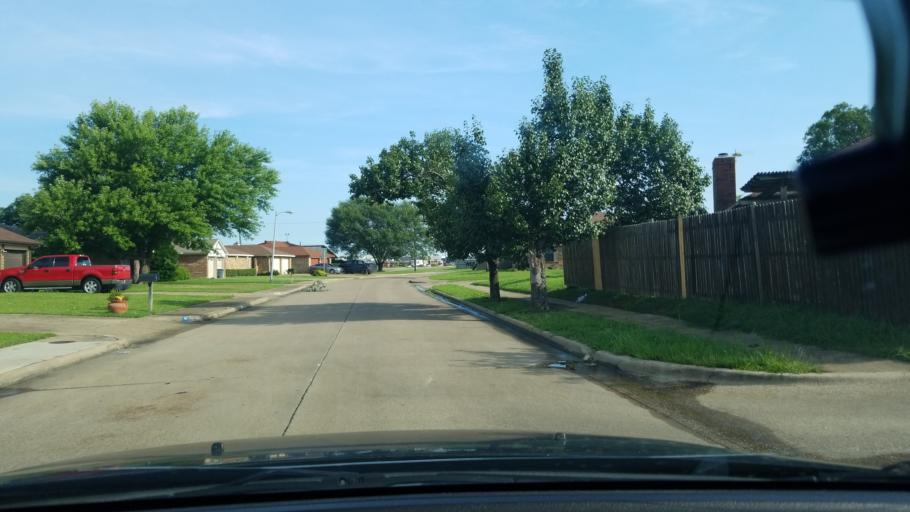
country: US
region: Texas
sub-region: Dallas County
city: Mesquite
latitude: 32.8040
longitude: -96.6092
